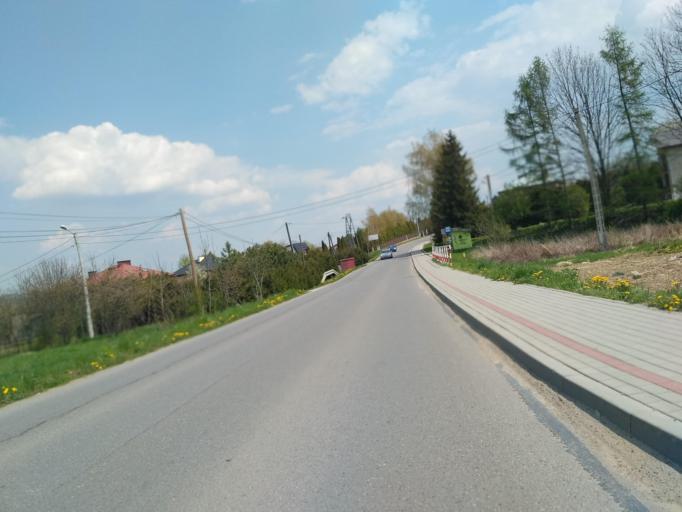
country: PL
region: Subcarpathian Voivodeship
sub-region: Powiat jasielski
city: Jaslo
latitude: 49.7316
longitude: 21.5102
